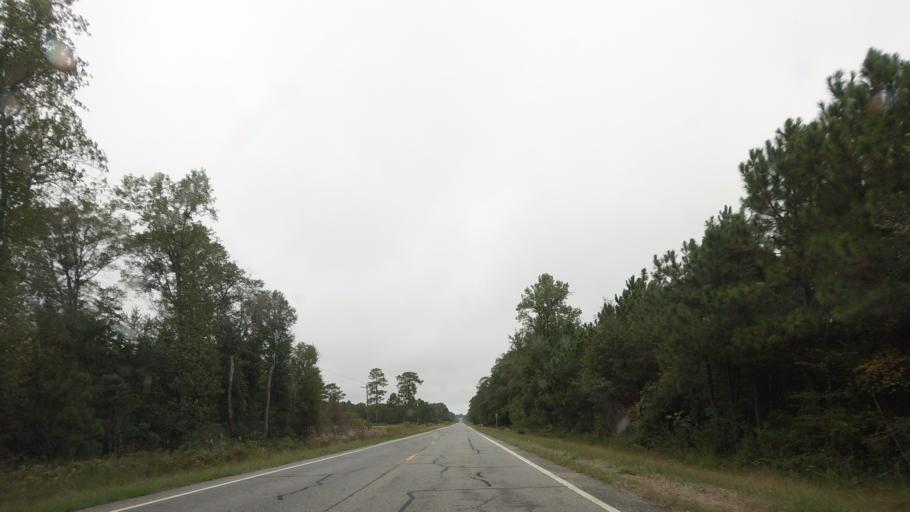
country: US
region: Georgia
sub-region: Irwin County
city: Ocilla
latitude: 31.4892
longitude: -83.2384
